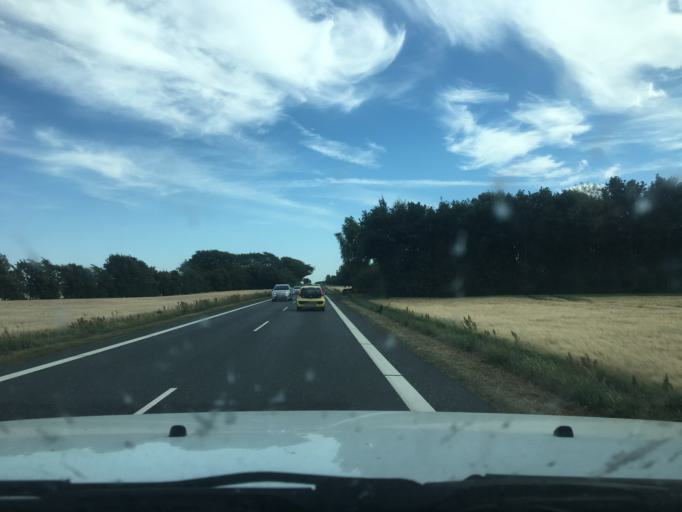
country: DK
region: Central Jutland
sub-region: Viborg Kommune
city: Viborg
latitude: 56.5916
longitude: 9.3658
